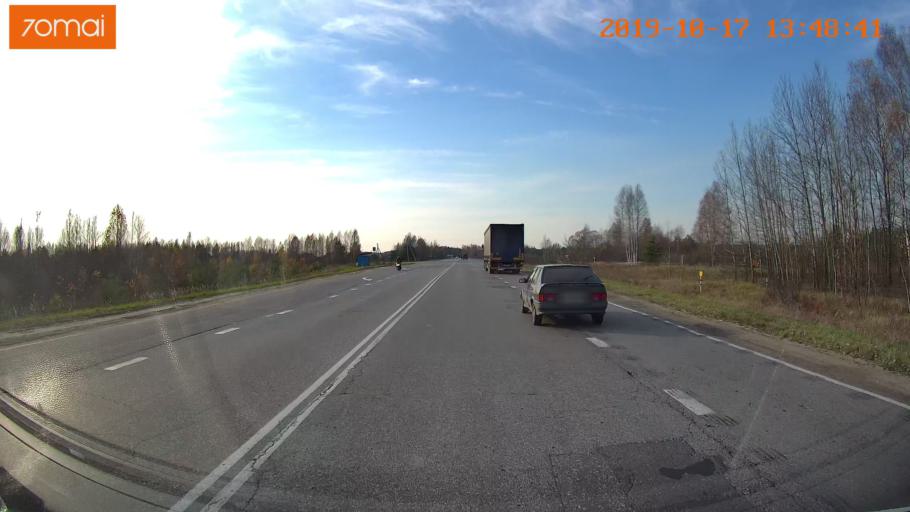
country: RU
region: Rjazan
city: Tuma
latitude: 55.1473
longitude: 40.4519
